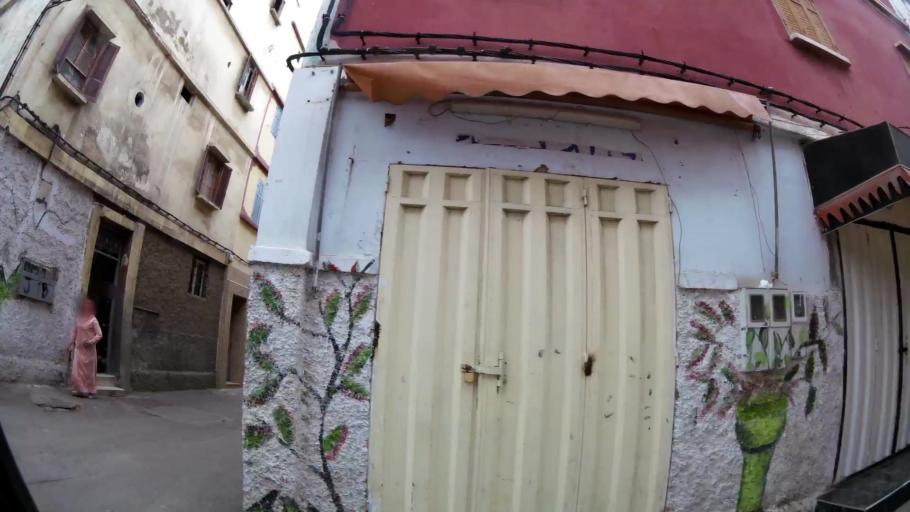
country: MA
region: Grand Casablanca
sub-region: Casablanca
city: Casablanca
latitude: 33.5835
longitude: -7.5595
